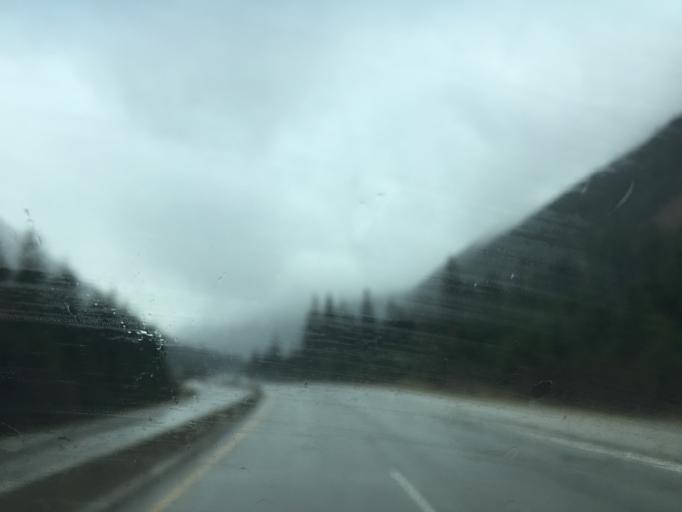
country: CA
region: British Columbia
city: Hope
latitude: 49.5528
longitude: -121.1926
